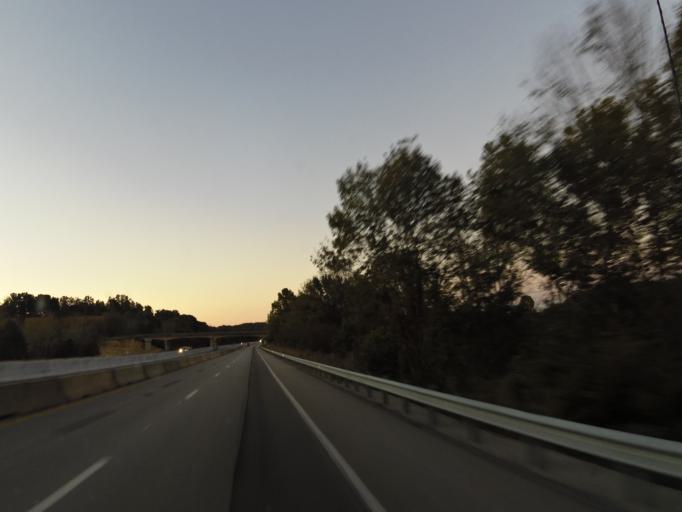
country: US
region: Kentucky
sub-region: Rockcastle County
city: Brodhead
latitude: 37.4645
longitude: -84.3351
